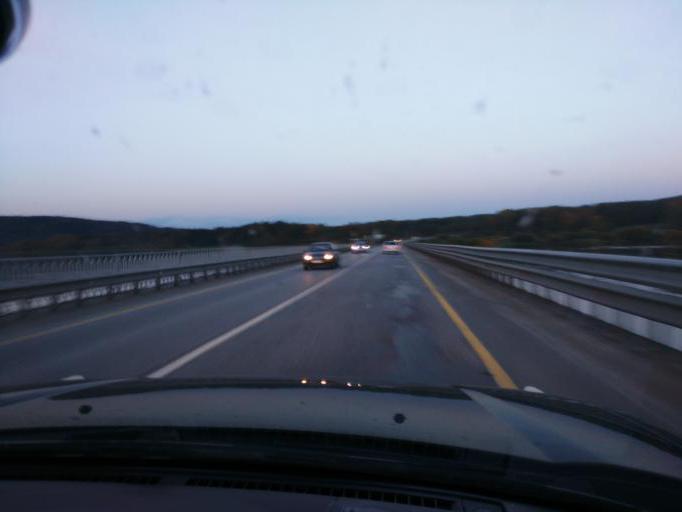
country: RU
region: Perm
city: Verkhnechusovskiye Gorodki
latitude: 58.2935
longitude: 56.8816
